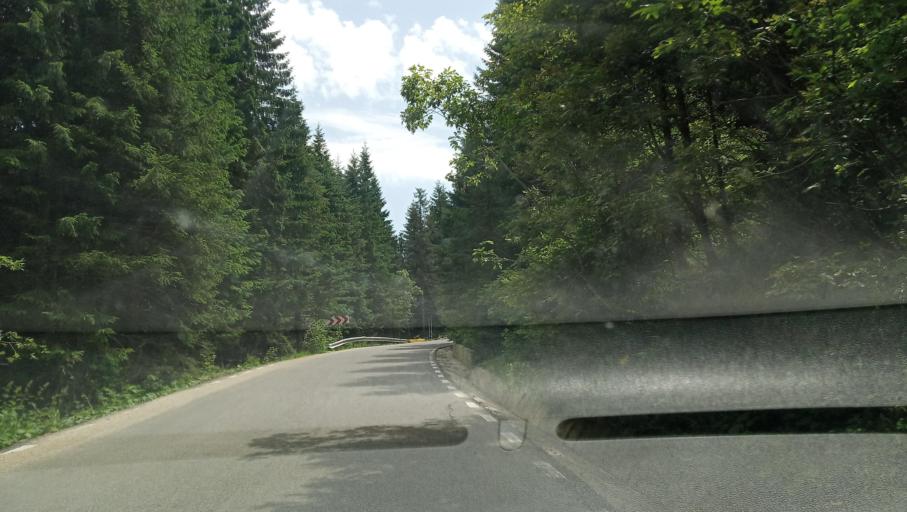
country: RO
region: Dambovita
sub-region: Comuna Moroeni
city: Glod
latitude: 45.3267
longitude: 25.4469
